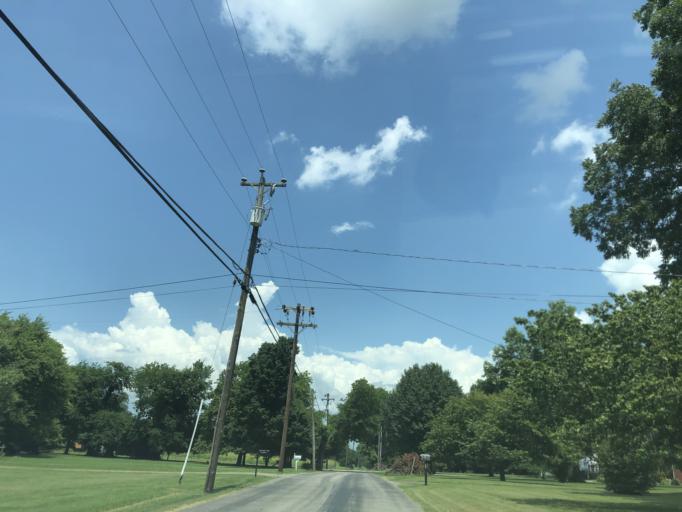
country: US
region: Tennessee
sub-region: Davidson County
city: Lakewood
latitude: 36.2043
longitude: -86.6194
